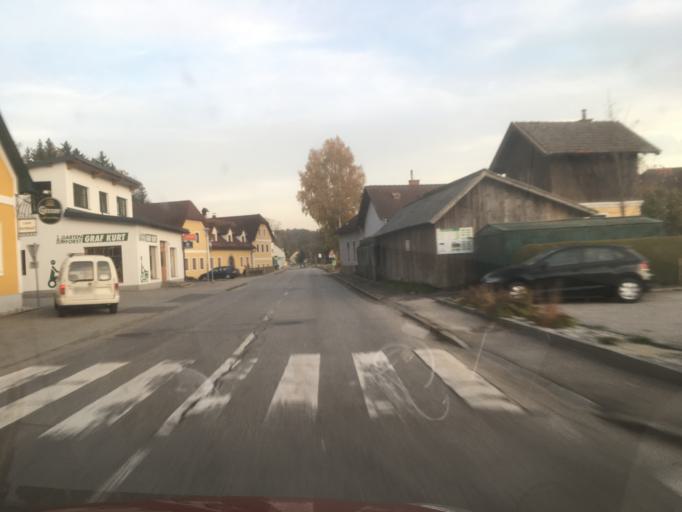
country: AT
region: Lower Austria
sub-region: Politischer Bezirk Zwettl
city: Langschlag
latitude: 48.5774
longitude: 14.8819
